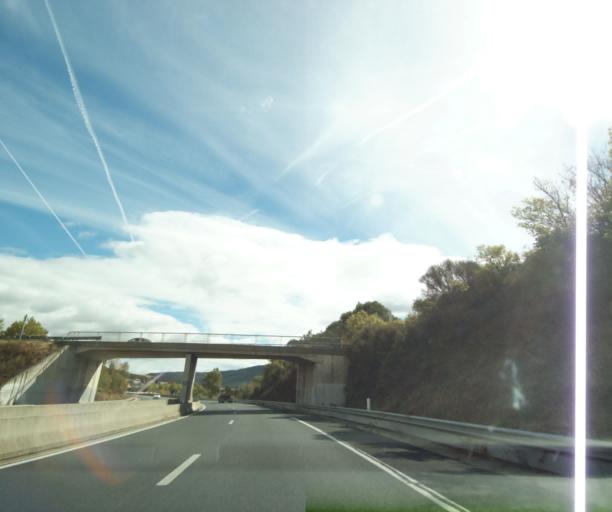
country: FR
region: Languedoc-Roussillon
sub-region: Departement de l'Herault
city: Lodeve
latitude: 43.6933
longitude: 3.3439
